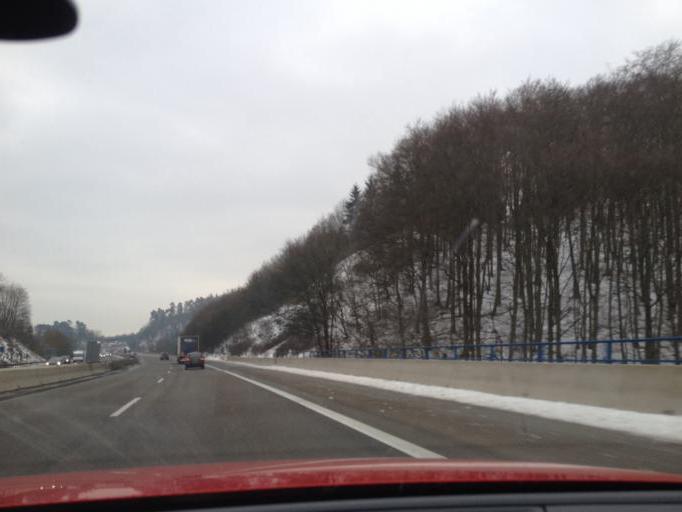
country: DE
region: Hesse
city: Herborn
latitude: 50.7059
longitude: 8.2876
